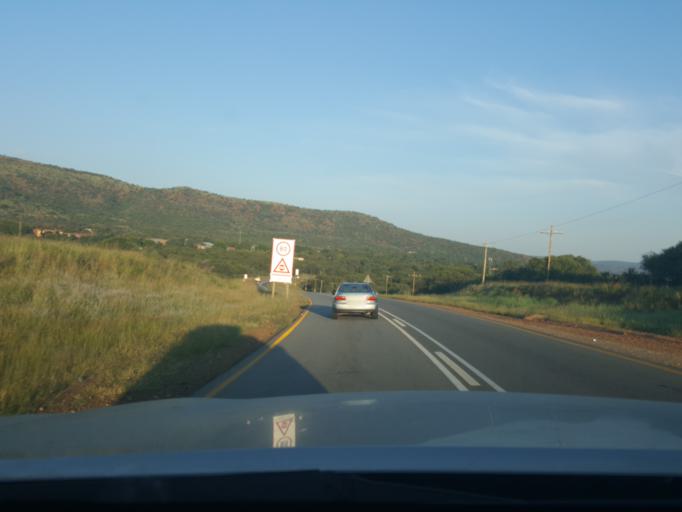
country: ZA
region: North-West
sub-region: Ngaka Modiri Molema District Municipality
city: Zeerust
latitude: -25.5222
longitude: 26.0691
